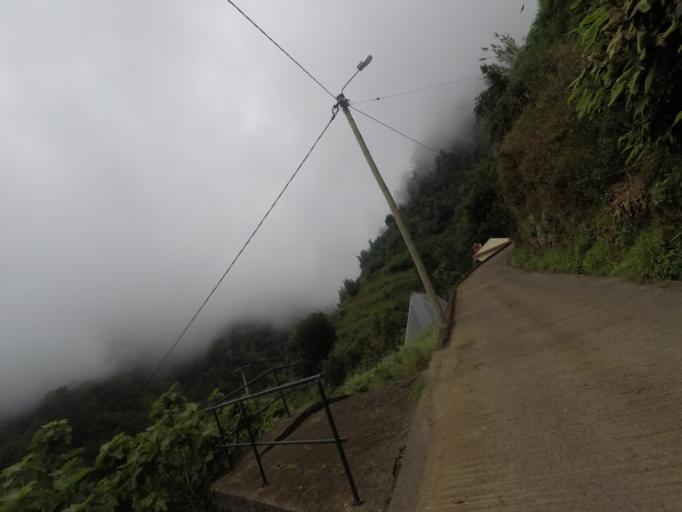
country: PT
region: Madeira
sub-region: Santana
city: Santana
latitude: 32.7736
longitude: -16.8788
